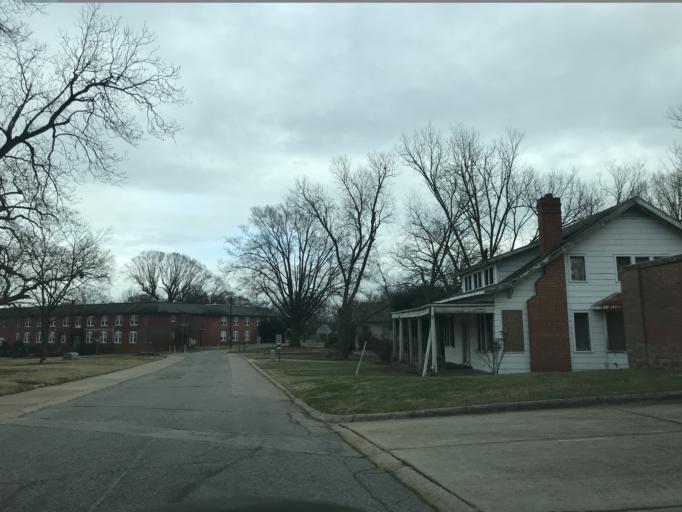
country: US
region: North Carolina
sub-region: Wake County
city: Raleigh
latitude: 35.7677
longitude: -78.6539
